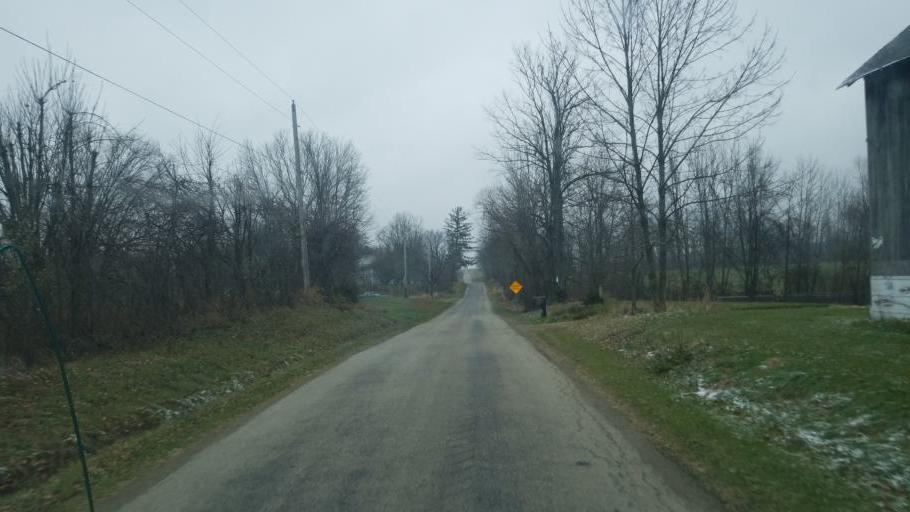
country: US
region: Ohio
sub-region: Huron County
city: New London
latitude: 41.0369
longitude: -82.3259
